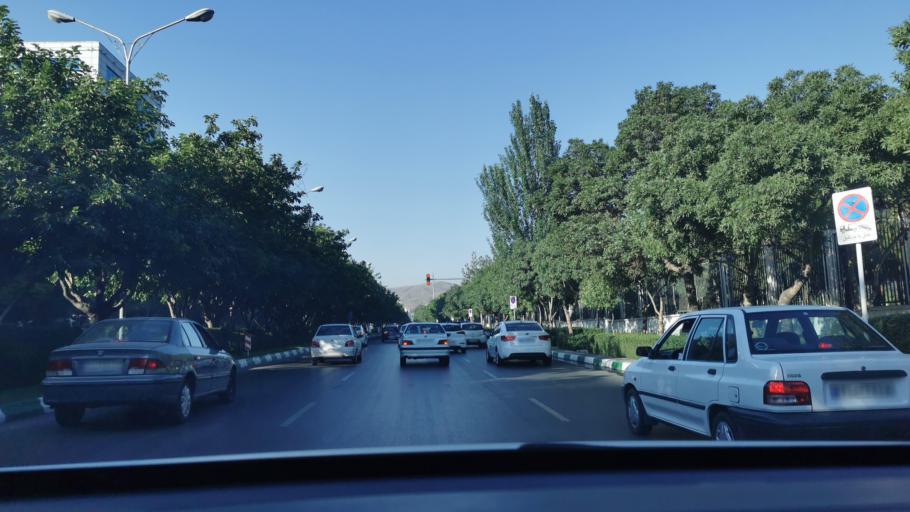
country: IR
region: Razavi Khorasan
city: Mashhad
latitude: 36.2957
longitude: 59.5609
